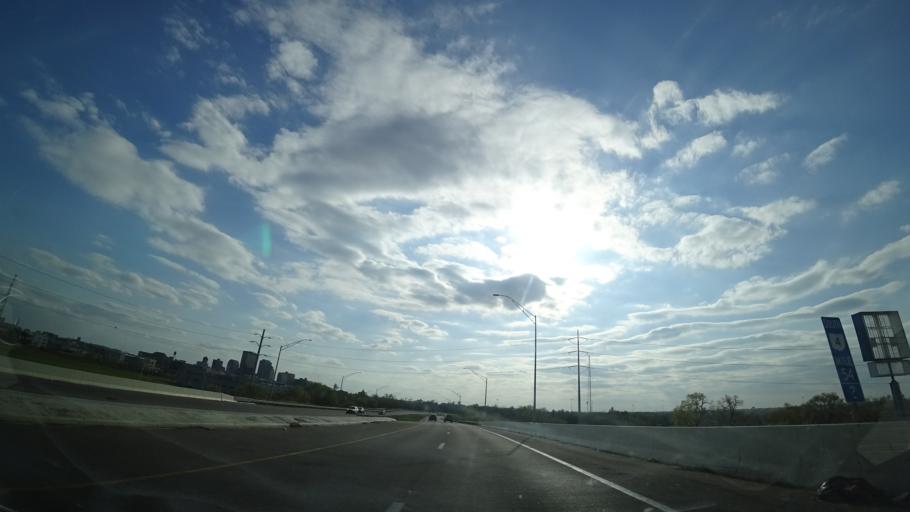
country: US
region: Ohio
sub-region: Montgomery County
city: Dayton
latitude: 39.7719
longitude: -84.1786
